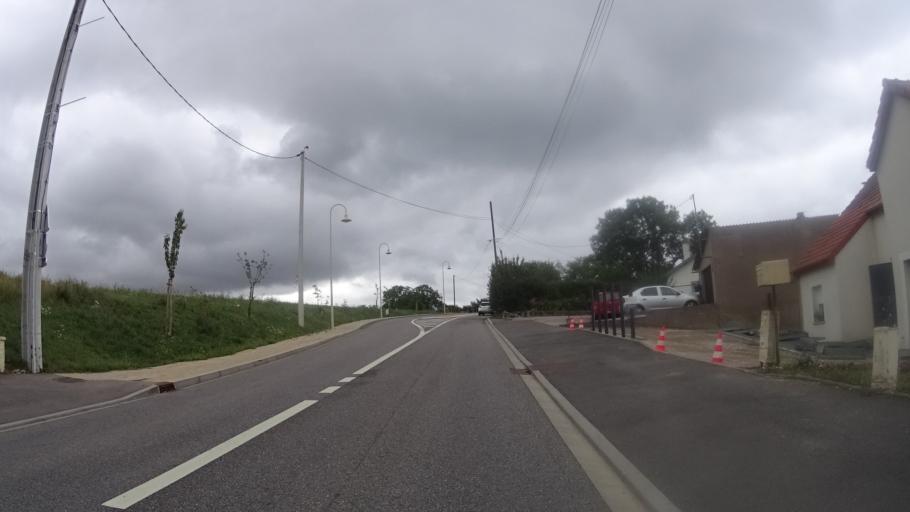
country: FR
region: Lorraine
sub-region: Departement de Meurthe-et-Moselle
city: Art-sur-Meurthe
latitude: 48.6524
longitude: 6.2695
